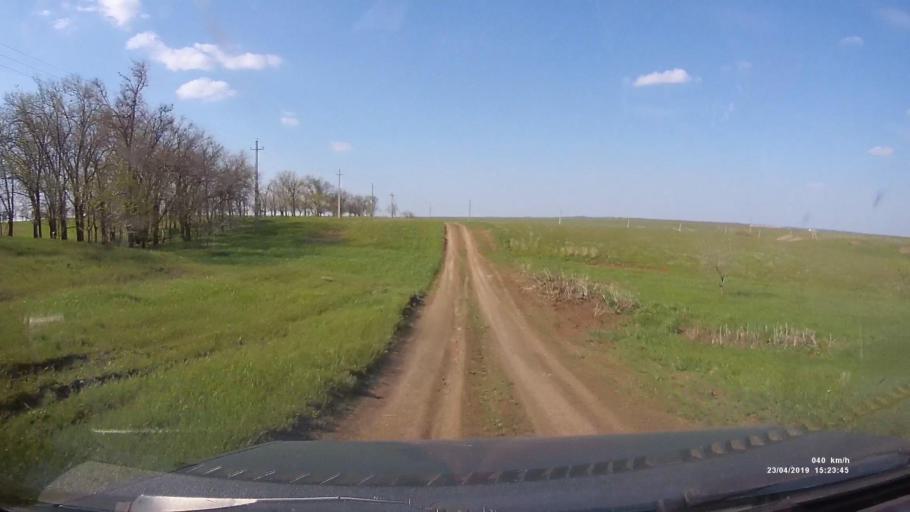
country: RU
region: Rostov
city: Remontnoye
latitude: 46.5375
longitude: 42.9697
